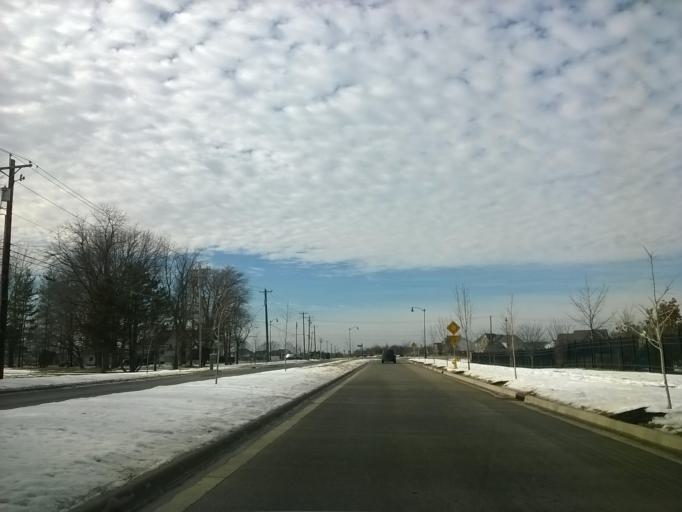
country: US
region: Indiana
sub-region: Boone County
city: Zionsville
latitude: 39.9773
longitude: -86.2196
